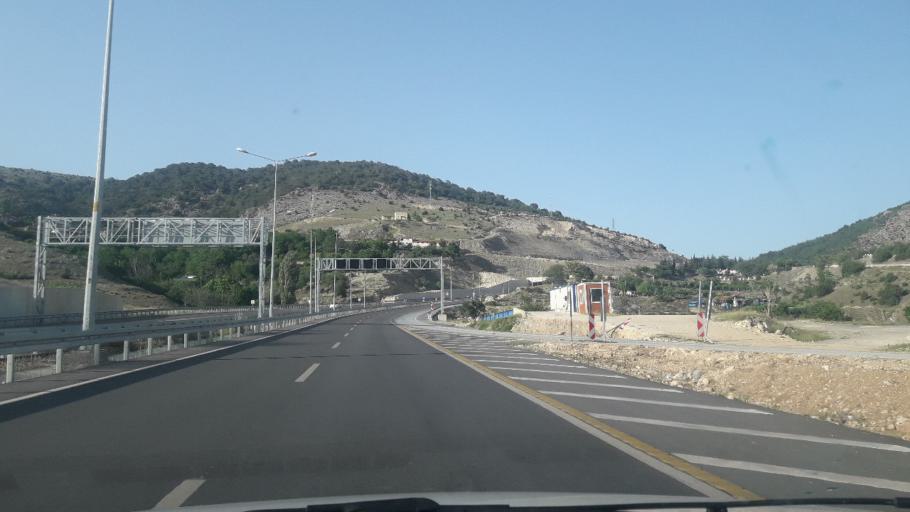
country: TR
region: Amasya
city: Amasya
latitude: 40.6607
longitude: 35.7887
